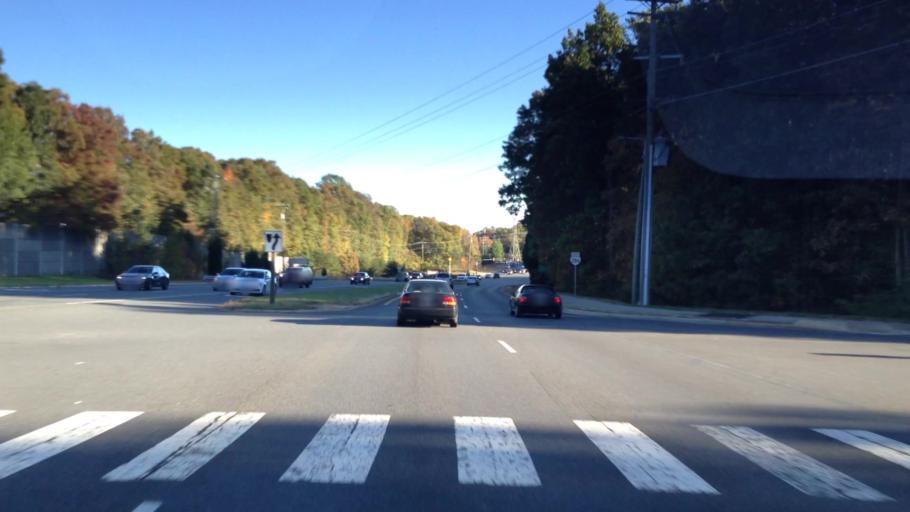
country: US
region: Virginia
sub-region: Fairfax County
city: Burke
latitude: 38.7584
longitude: -77.2793
